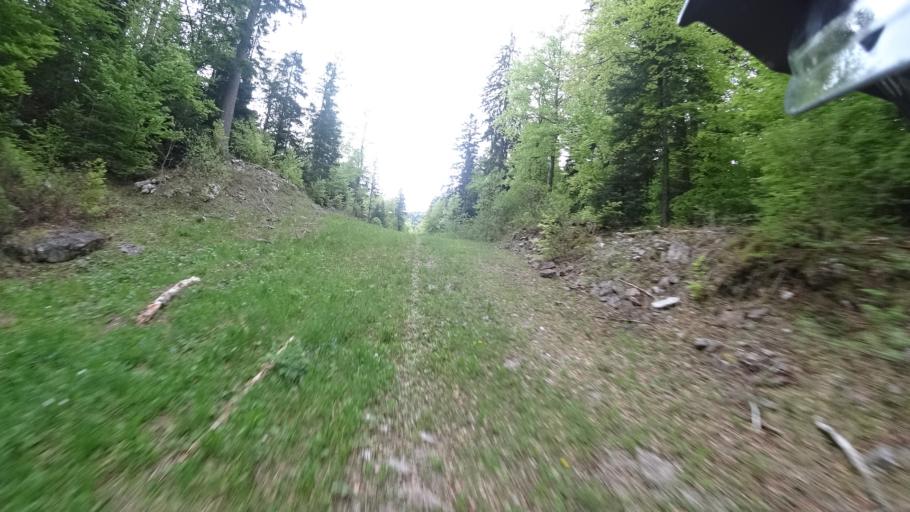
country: HR
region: Karlovacka
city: Plaski
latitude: 44.9294
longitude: 15.4238
